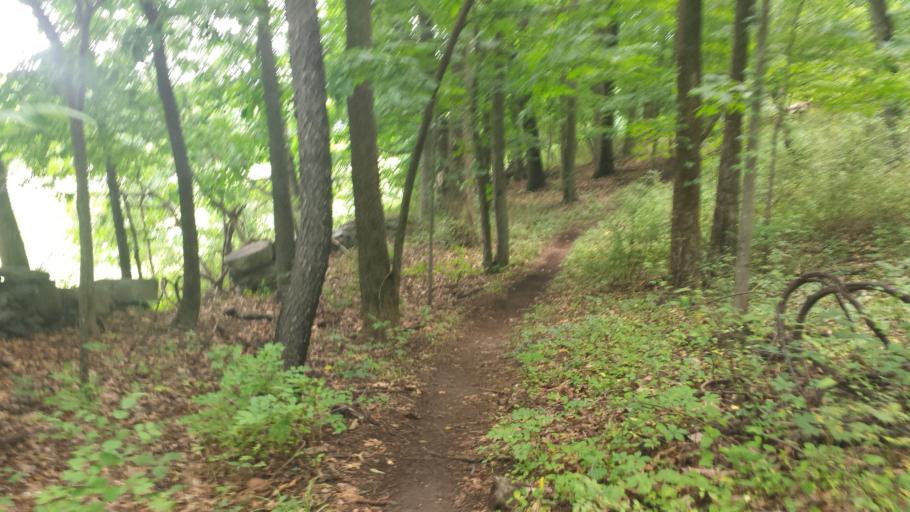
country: US
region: New York
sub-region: Westchester County
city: Hawthorne
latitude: 41.1121
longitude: -73.7989
